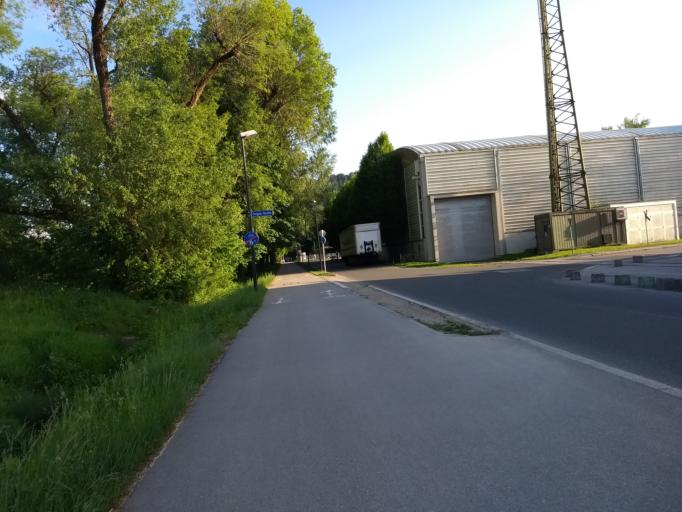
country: AT
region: Salzburg
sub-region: Salzburg Stadt
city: Salzburg
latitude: 47.8171
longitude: 13.0620
